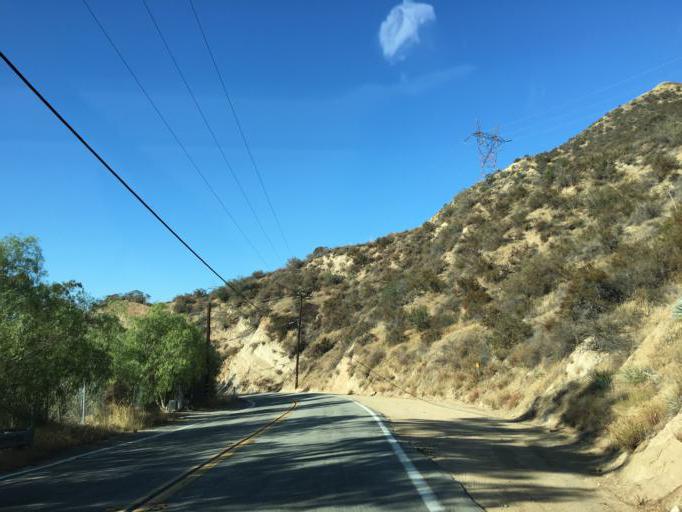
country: US
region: California
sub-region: Los Angeles County
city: San Fernando
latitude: 34.3240
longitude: -118.3386
